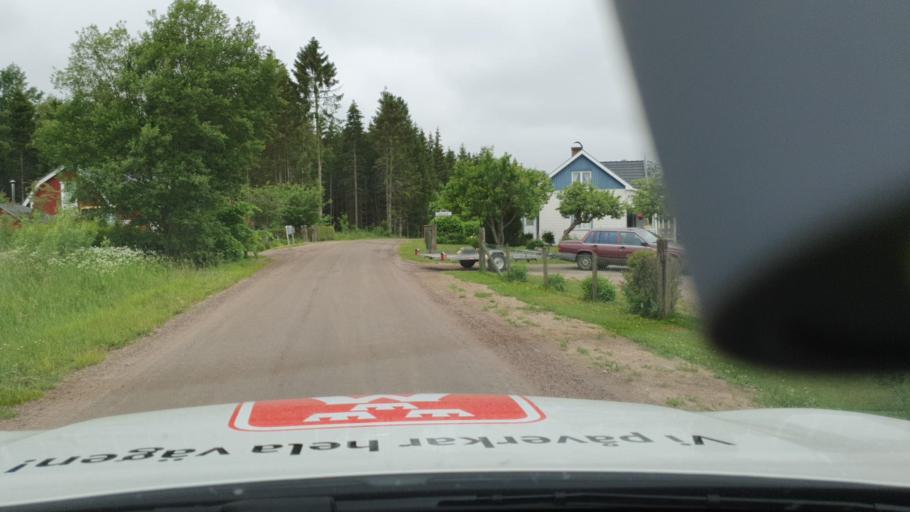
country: SE
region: Vaestra Goetaland
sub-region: Tidaholms Kommun
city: Olofstorp
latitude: 58.3550
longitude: 14.0437
